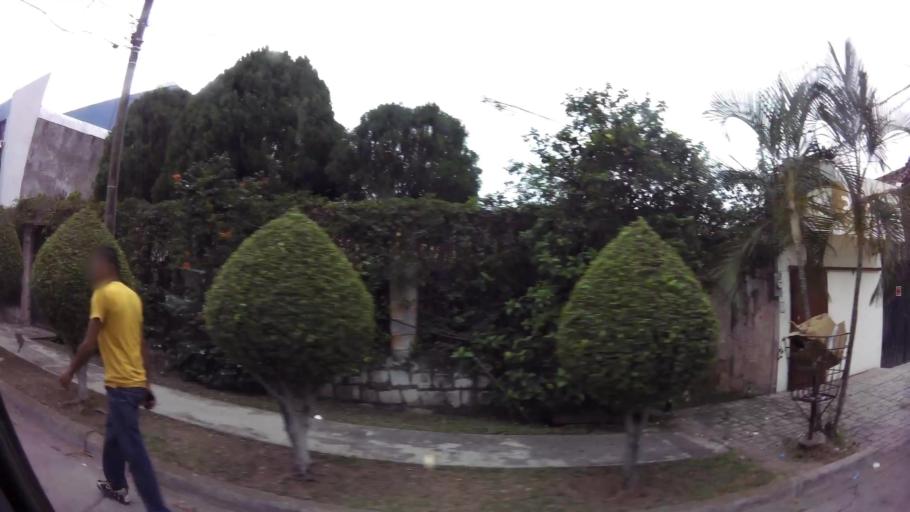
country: HN
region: Francisco Morazan
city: Tegucigalpa
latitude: 14.0918
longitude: -87.1915
